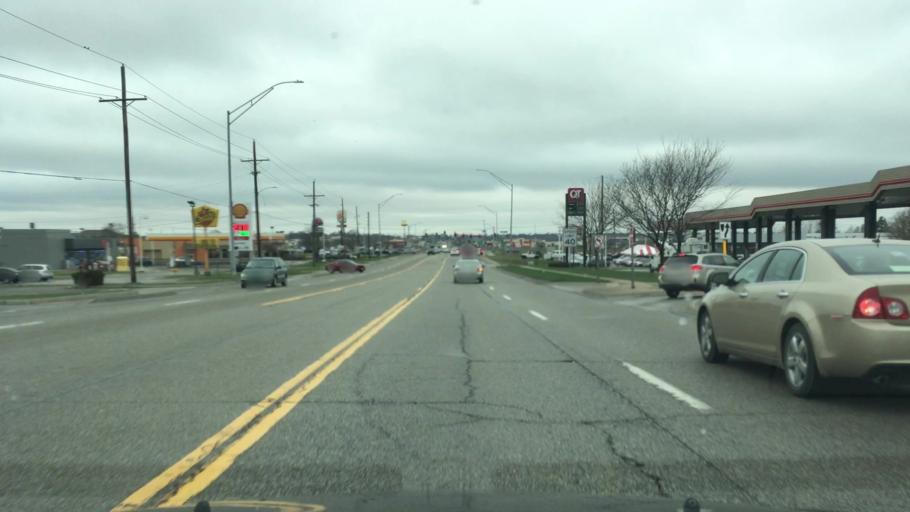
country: US
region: Missouri
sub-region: Cass County
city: Belton
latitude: 38.8132
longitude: -94.4986
